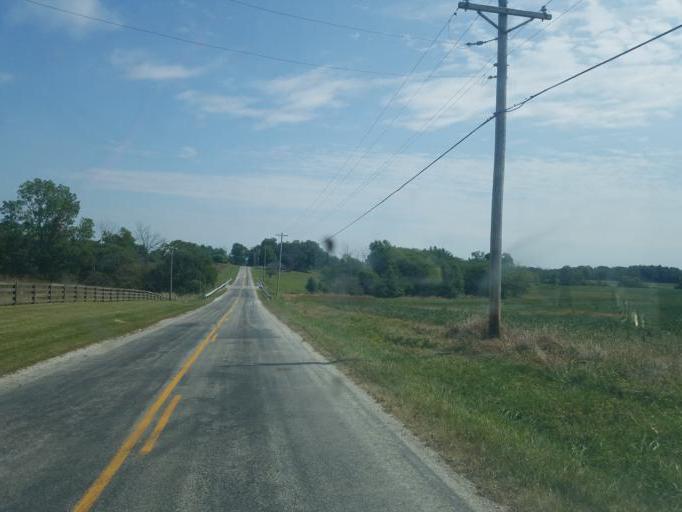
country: US
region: Ohio
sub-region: Marion County
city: Marion
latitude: 40.6878
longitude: -83.2336
